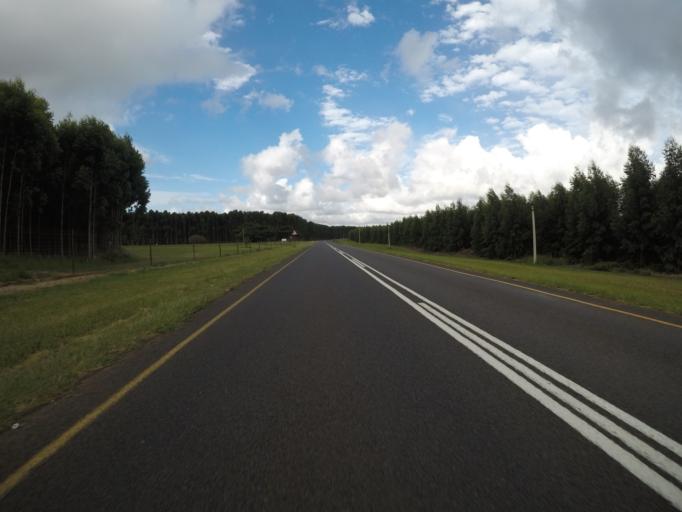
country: ZA
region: KwaZulu-Natal
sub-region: uMkhanyakude District Municipality
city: Mtubatuba
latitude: -28.3688
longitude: 32.2587
